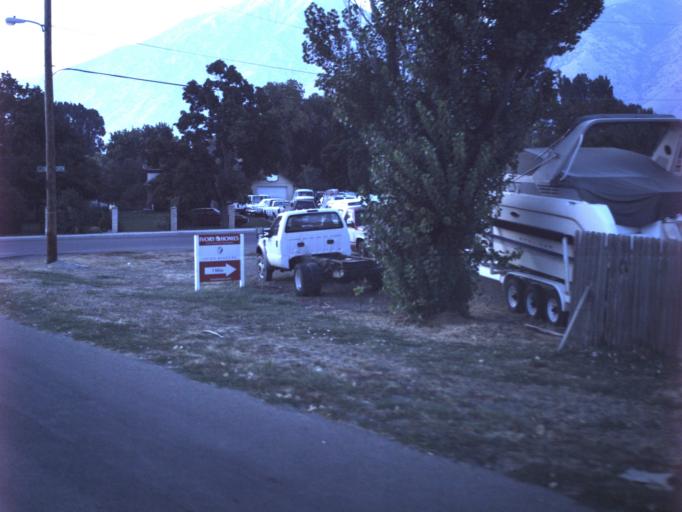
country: US
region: Utah
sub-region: Utah County
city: Springville
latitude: 40.1444
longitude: -111.6025
